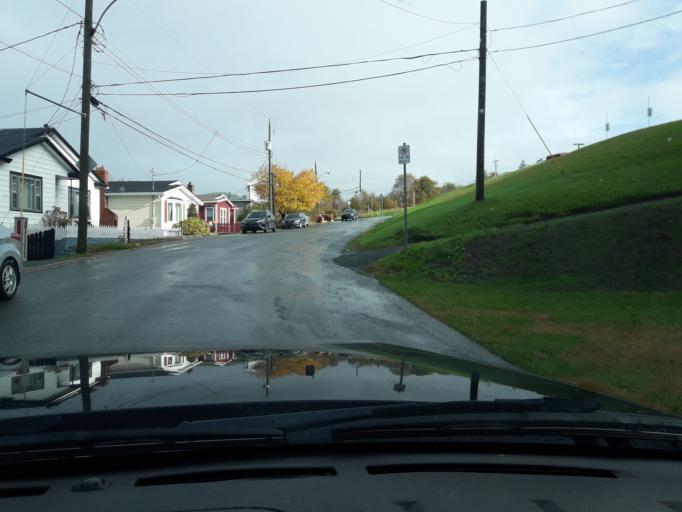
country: CA
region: Newfoundland and Labrador
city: St. John's
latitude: 47.5719
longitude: -52.6948
